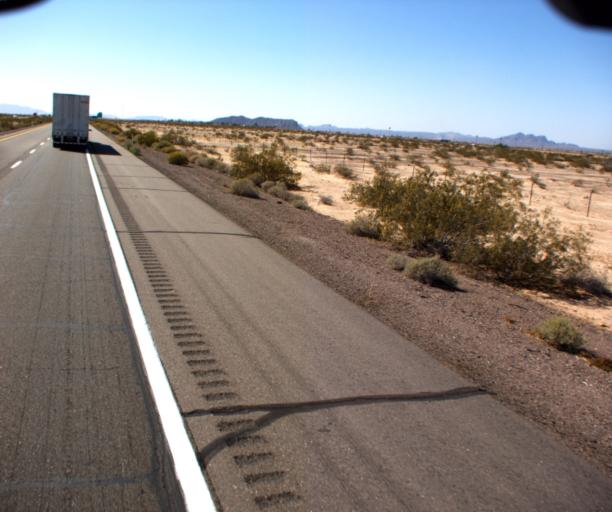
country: US
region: Arizona
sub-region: Yuma County
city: Wellton
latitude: 32.6981
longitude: -113.9245
